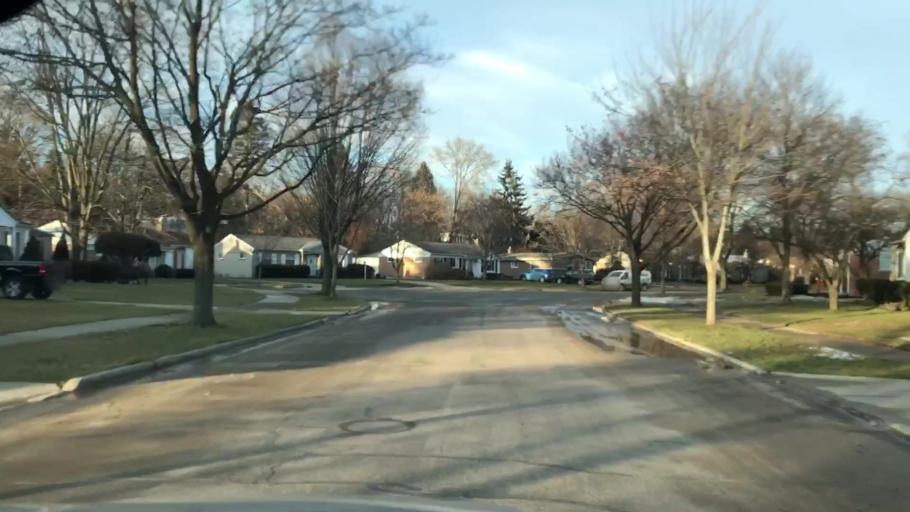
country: US
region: Michigan
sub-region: Wayne County
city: Northville
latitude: 42.4414
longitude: -83.4773
